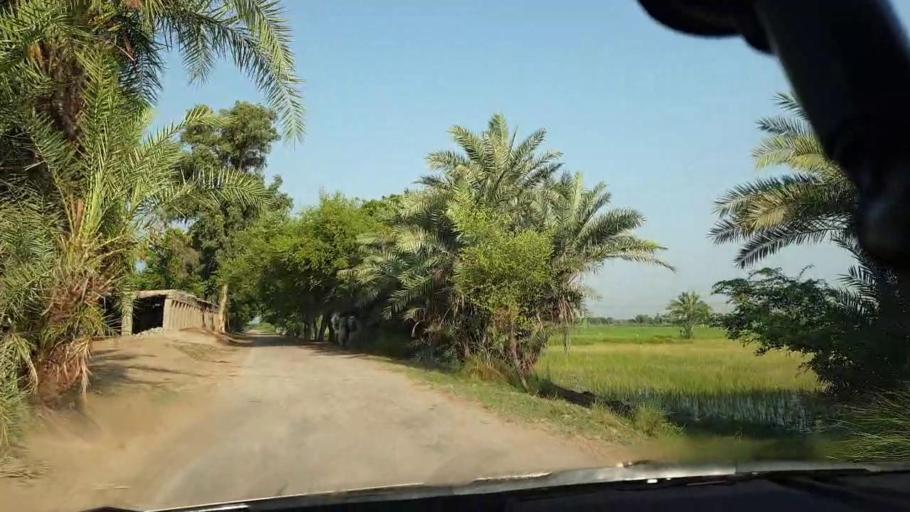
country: PK
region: Sindh
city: Larkana
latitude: 27.6198
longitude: 68.2124
